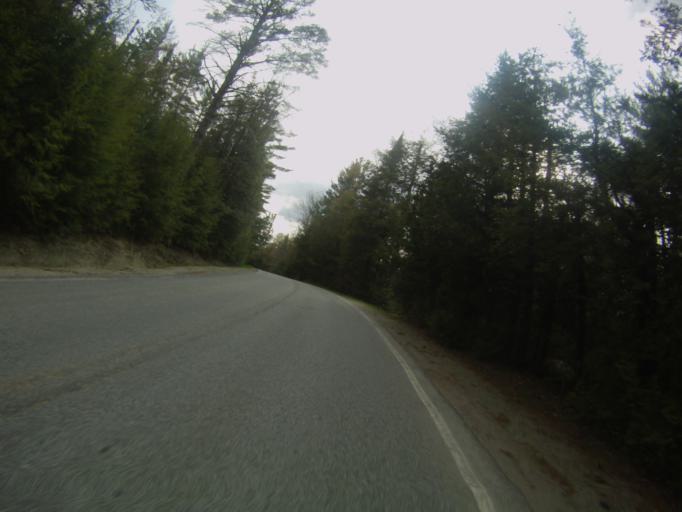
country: US
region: New York
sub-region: Warren County
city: Warrensburg
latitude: 43.8453
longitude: -73.8230
